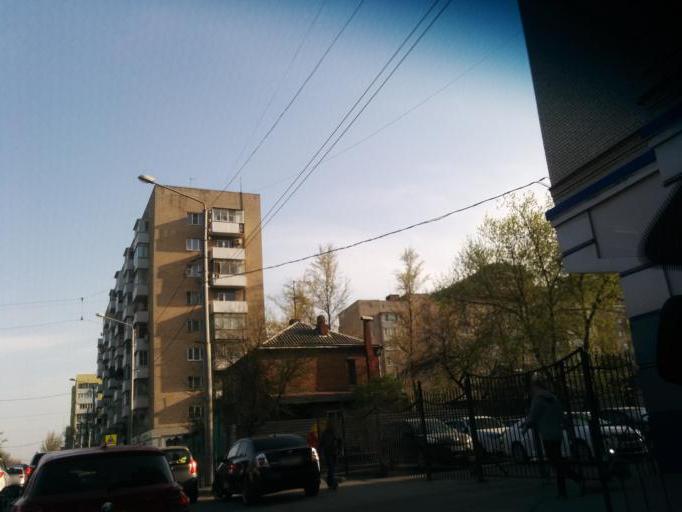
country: RU
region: Rostov
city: Rostov-na-Donu
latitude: 47.2333
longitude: 39.7394
